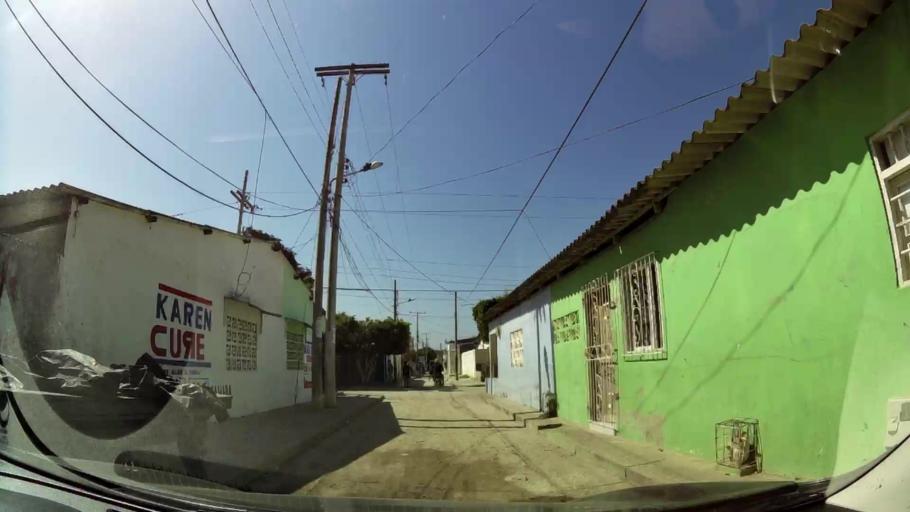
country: CO
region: Bolivar
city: Cartagena
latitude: 10.4400
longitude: -75.5143
